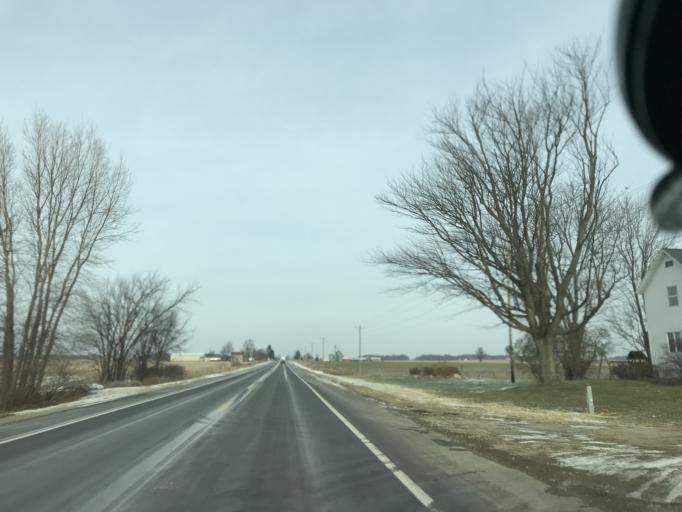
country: US
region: Michigan
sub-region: Ionia County
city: Lake Odessa
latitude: 42.8160
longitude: -85.0747
